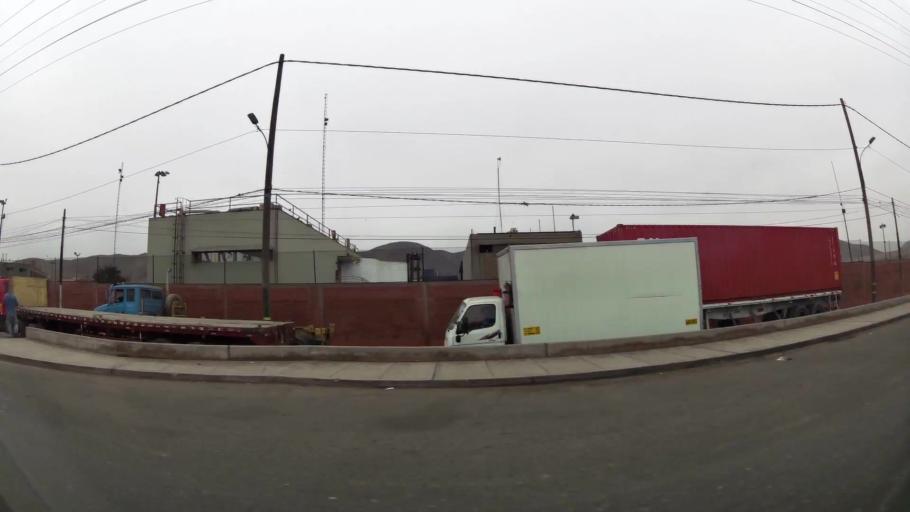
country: PE
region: Lima
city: Ventanilla
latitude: -11.9521
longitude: -77.1306
